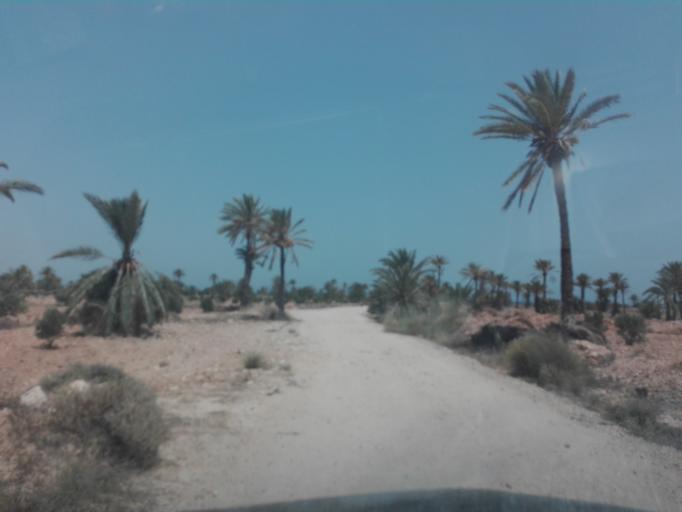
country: TN
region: Safaqis
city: Al Qarmadah
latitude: 34.6648
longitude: 11.0927
